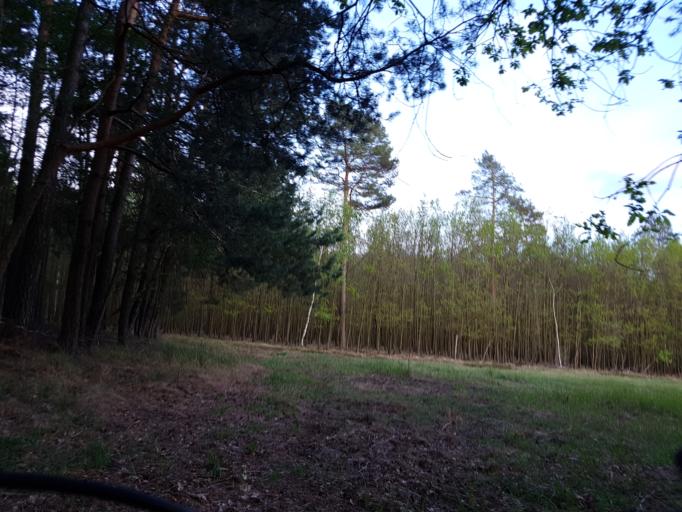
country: DE
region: Brandenburg
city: Schilda
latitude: 51.5724
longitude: 13.3807
